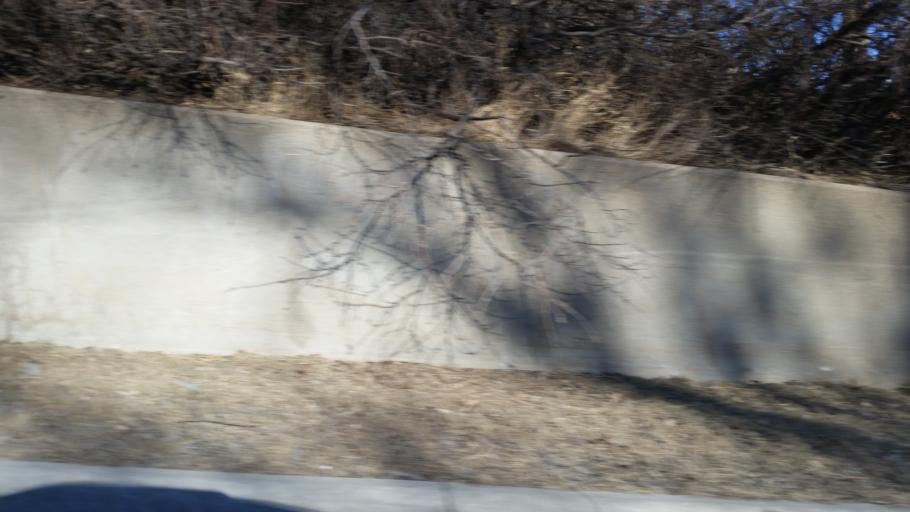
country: US
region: Nebraska
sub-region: Douglas County
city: Omaha
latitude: 41.1991
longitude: -95.9336
